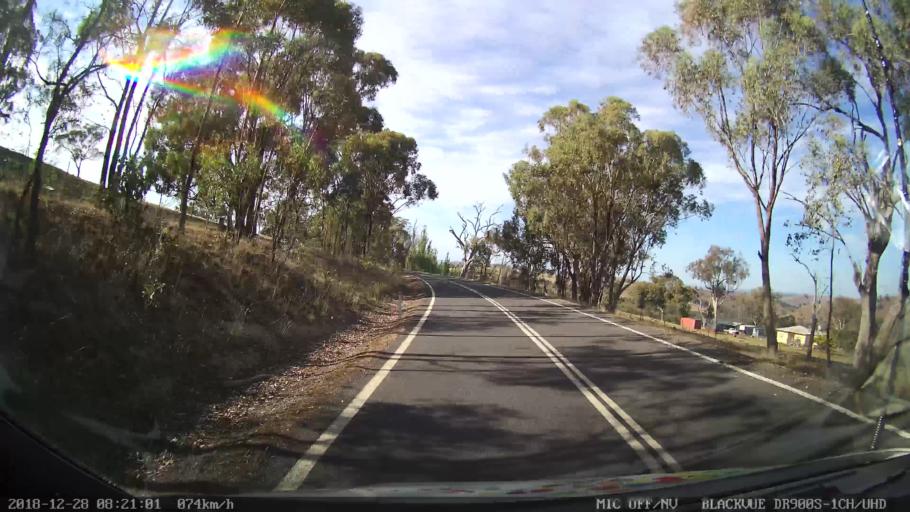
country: AU
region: New South Wales
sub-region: Blayney
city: Blayney
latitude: -33.8779
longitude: 149.3504
